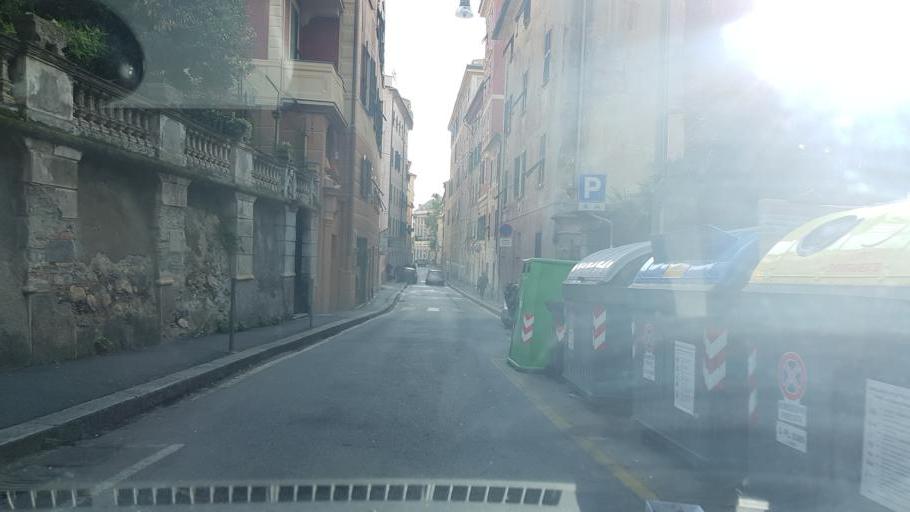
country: IT
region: Liguria
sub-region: Provincia di Genova
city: Bogliasco
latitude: 44.3834
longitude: 9.0434
